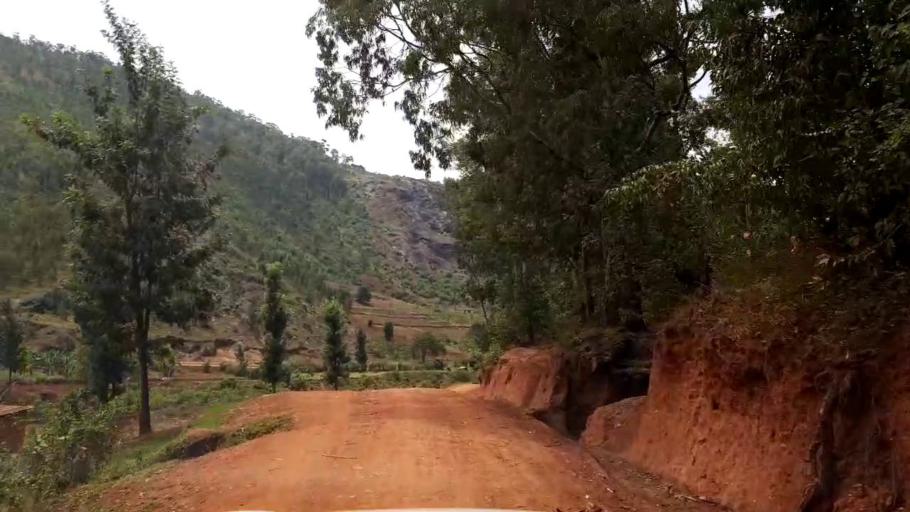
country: RW
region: Northern Province
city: Byumba
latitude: -1.5120
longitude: 30.1934
